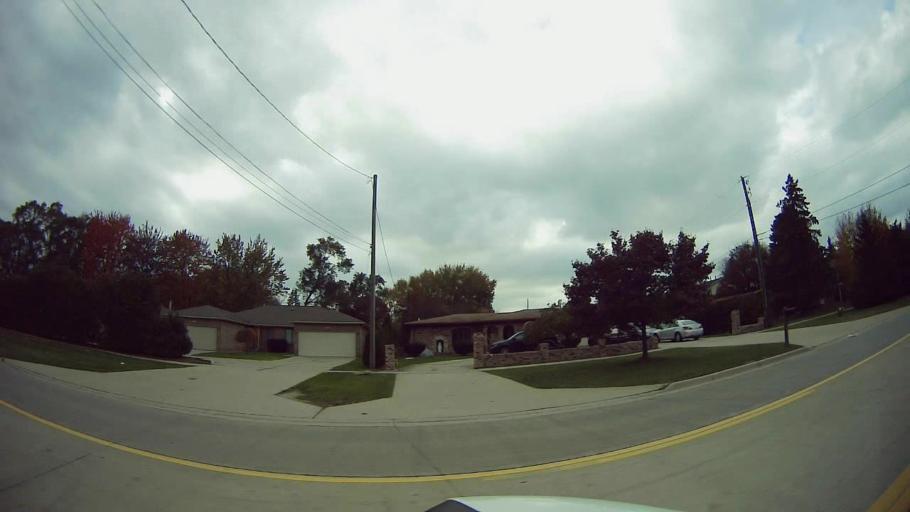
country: US
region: Michigan
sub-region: Macomb County
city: Sterling Heights
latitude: 42.5492
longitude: -83.0044
